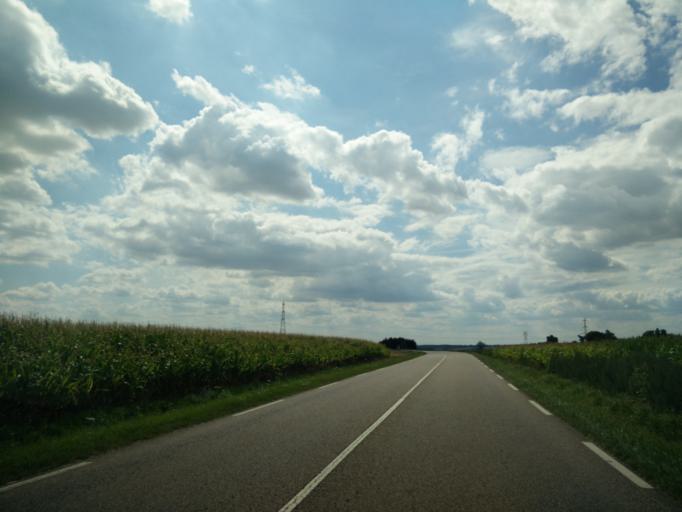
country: FR
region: Ile-de-France
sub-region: Departement des Yvelines
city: Guerville
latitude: 48.9352
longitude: 1.7238
